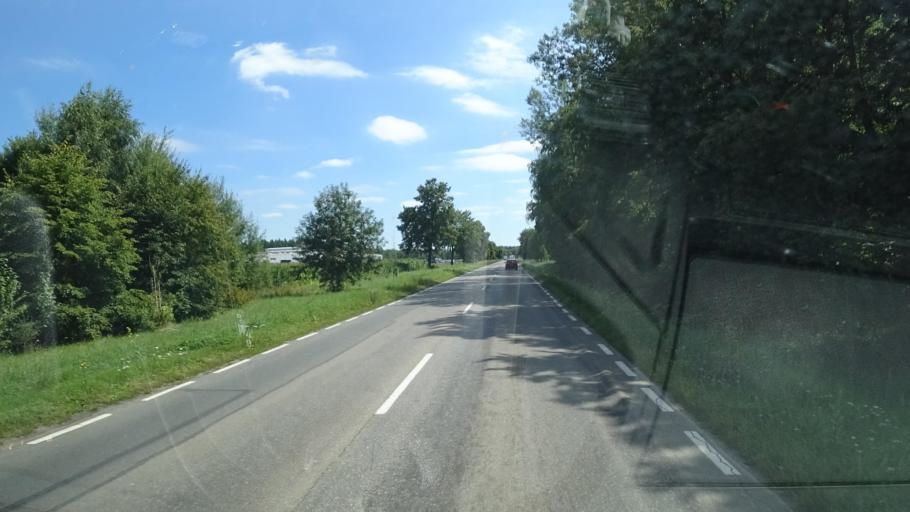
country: PL
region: Warmian-Masurian Voivodeship
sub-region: Powiat elcki
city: Prostki
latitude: 53.7238
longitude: 22.3857
